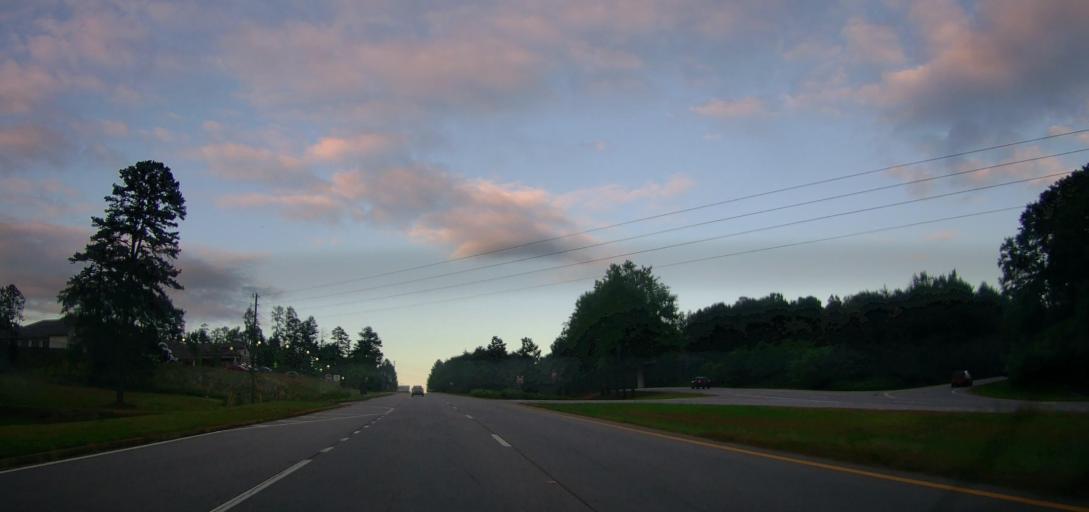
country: US
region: Georgia
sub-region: Clarke County
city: Country Club Estates
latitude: 33.9452
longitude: -83.4351
